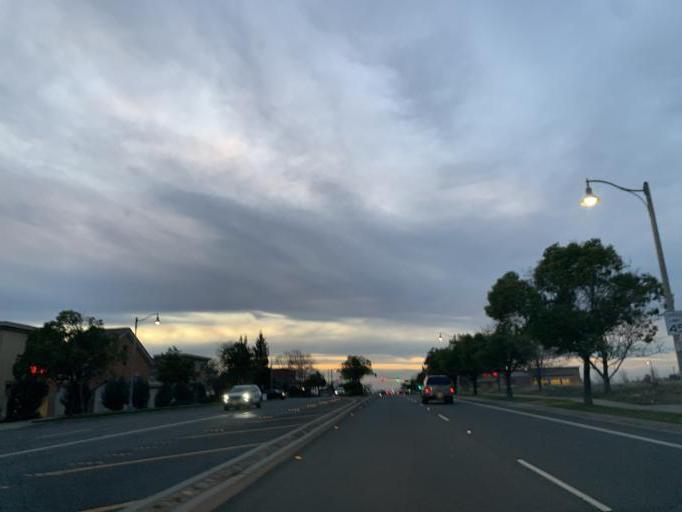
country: US
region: California
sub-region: Placer County
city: Lincoln
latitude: 38.8513
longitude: -121.2854
